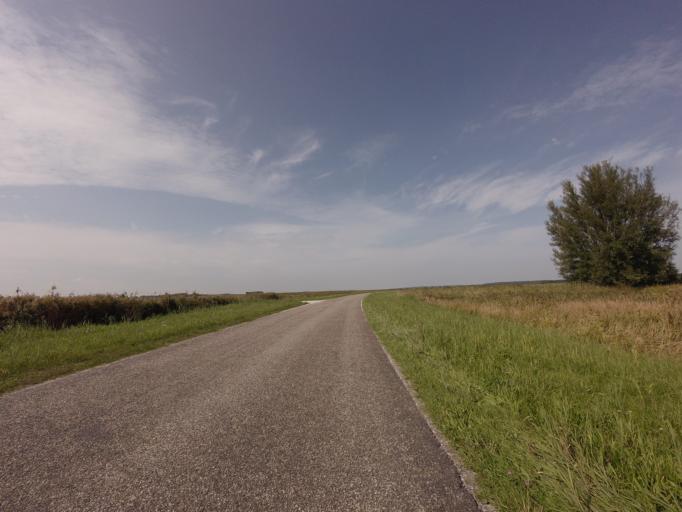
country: NL
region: Groningen
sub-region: Gemeente De Marne
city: Ulrum
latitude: 53.3471
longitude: 6.2697
